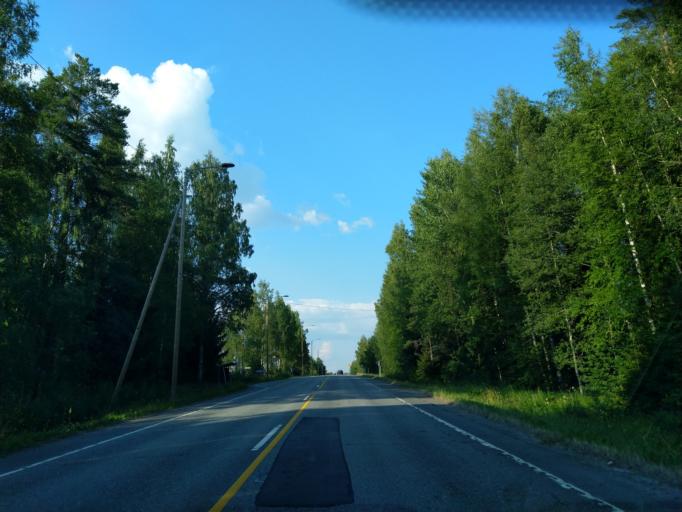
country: FI
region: Satakunta
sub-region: Pori
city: Laengelmaeki
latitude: 61.7582
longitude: 22.1356
